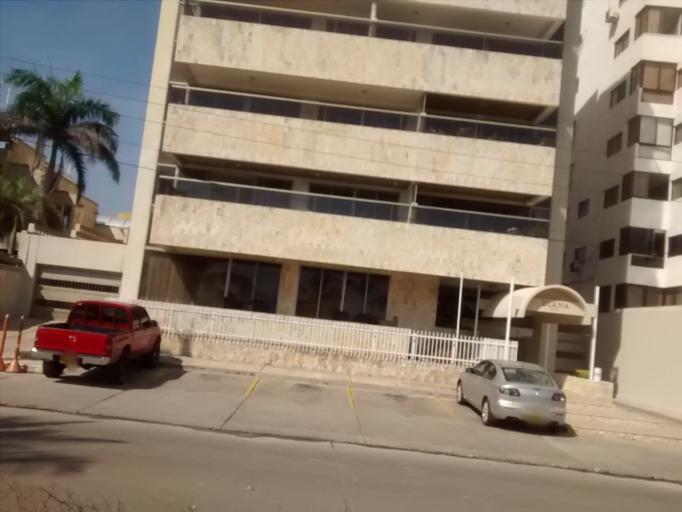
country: CO
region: Bolivar
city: Cartagena
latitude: 10.3932
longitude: -75.5473
